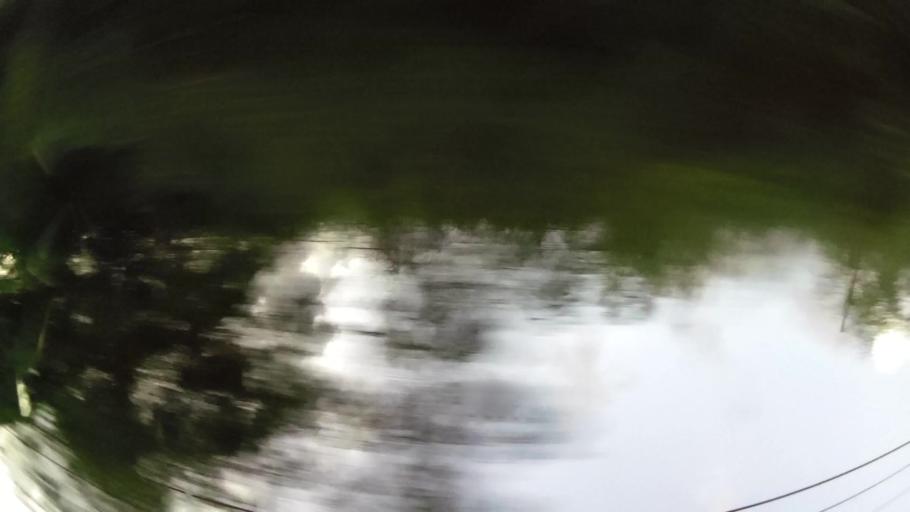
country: BB
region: Saint John
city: Four Cross Roads
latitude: 13.1198
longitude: -59.5147
